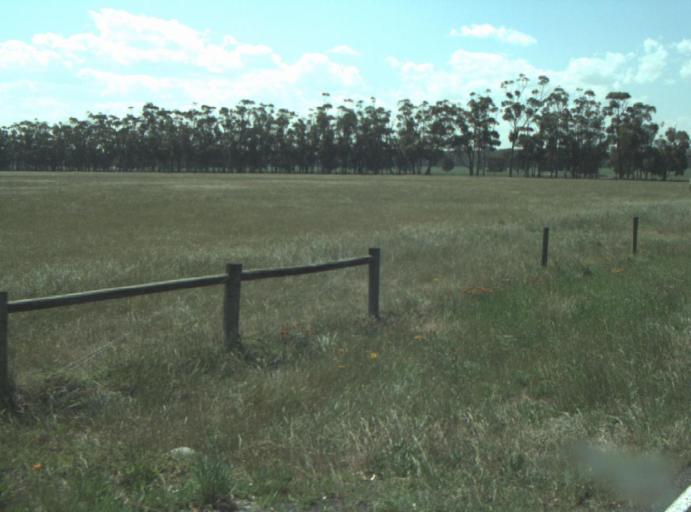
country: AU
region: Victoria
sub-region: Greater Geelong
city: Lara
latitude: -37.9747
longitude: 144.4050
